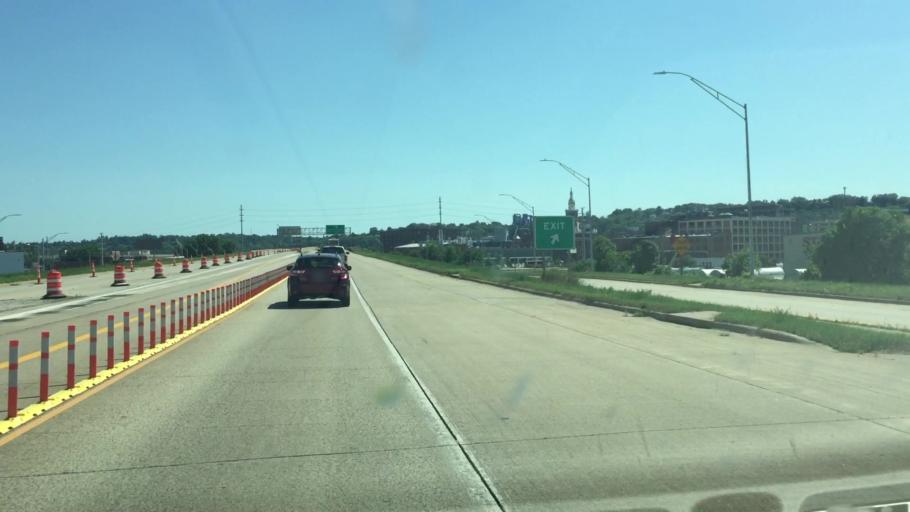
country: US
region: Iowa
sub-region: Dubuque County
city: Dubuque
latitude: 42.5080
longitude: -90.6596
